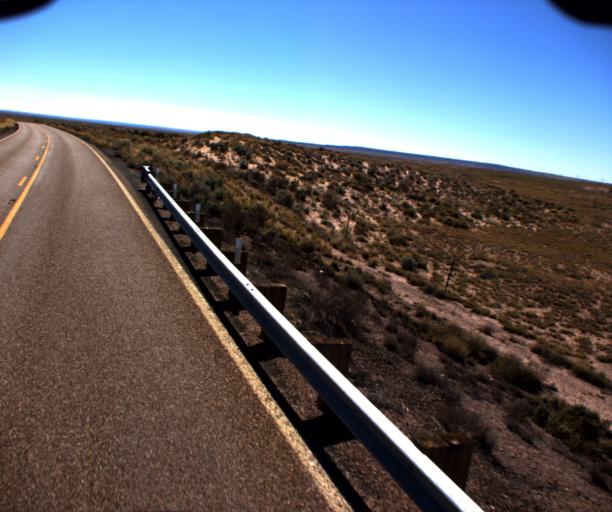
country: US
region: Arizona
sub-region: Navajo County
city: Holbrook
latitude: 35.1434
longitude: -110.0890
